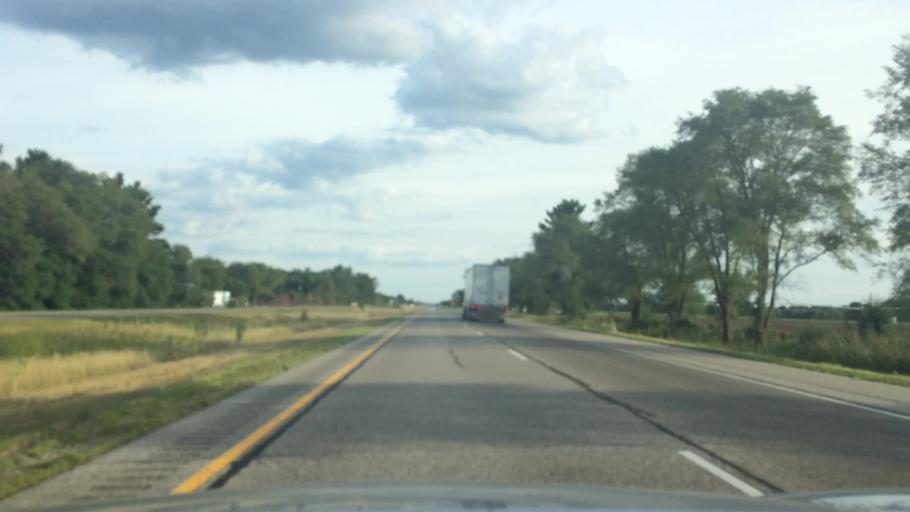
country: US
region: Wisconsin
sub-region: Portage County
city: Plover
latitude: 44.2483
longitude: -89.5242
